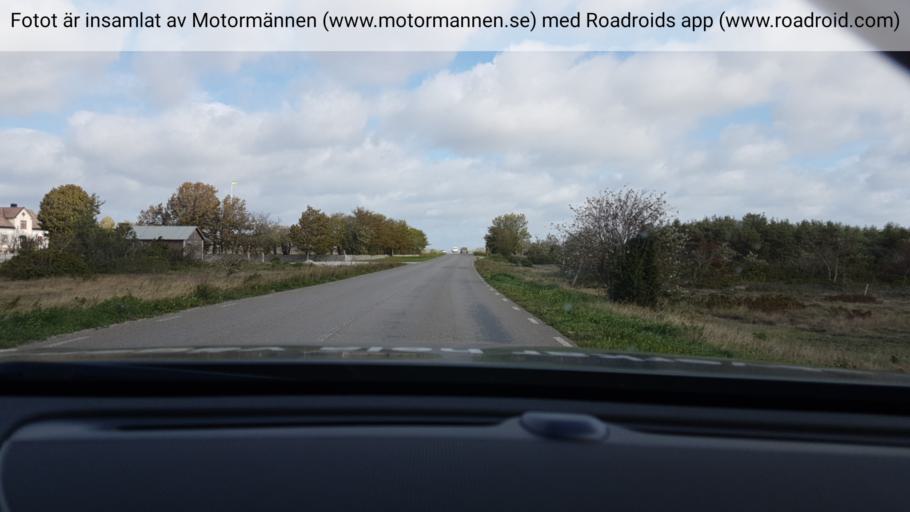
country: SE
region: Gotland
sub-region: Gotland
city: Slite
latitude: 57.9208
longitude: 19.1392
